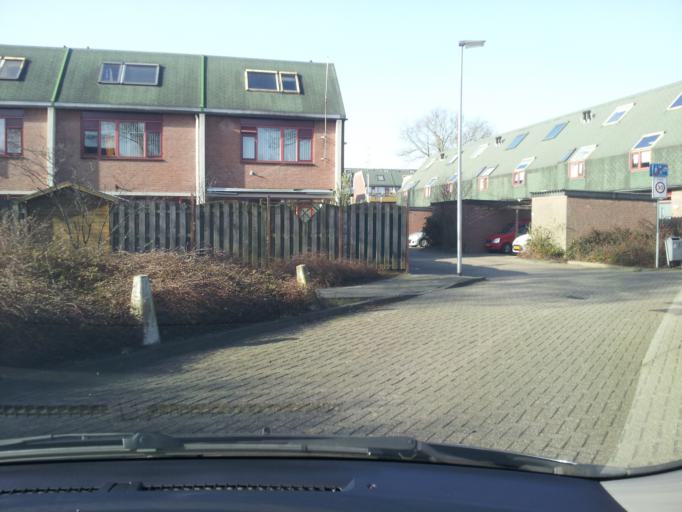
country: NL
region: South Holland
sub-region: Gemeente Zoetermeer
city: Zoetermeer
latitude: 52.0694
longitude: 4.4753
